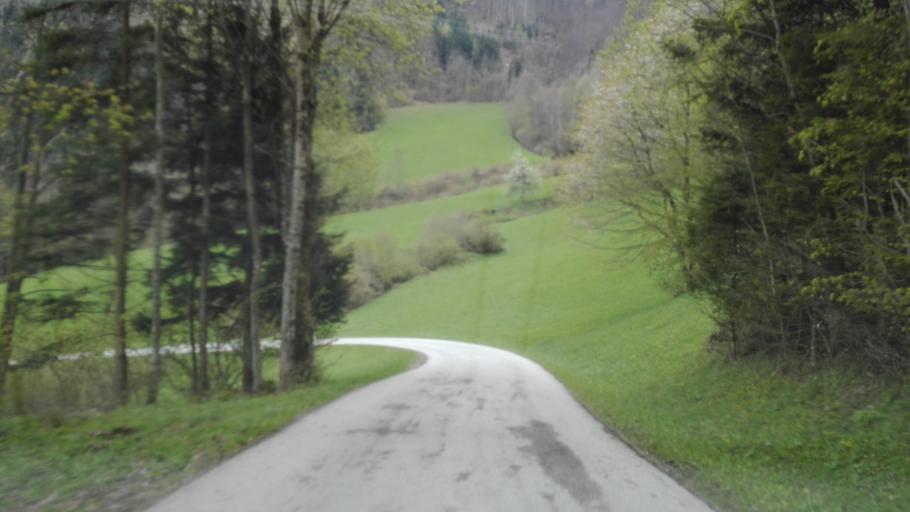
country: AT
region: Upper Austria
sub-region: Politischer Bezirk Steyr-Land
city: Ternberg
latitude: 47.9209
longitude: 14.3186
